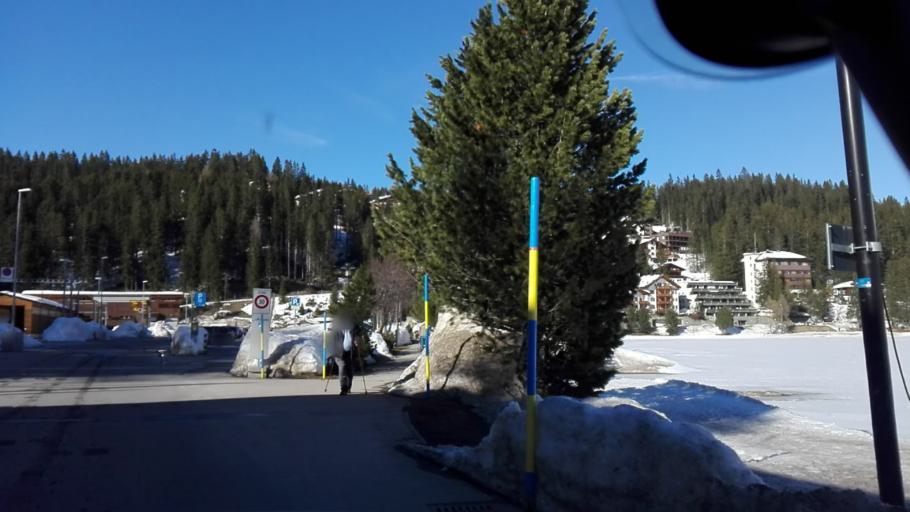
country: CH
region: Grisons
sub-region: Plessur District
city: Arosa
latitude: 46.7842
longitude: 9.6799
